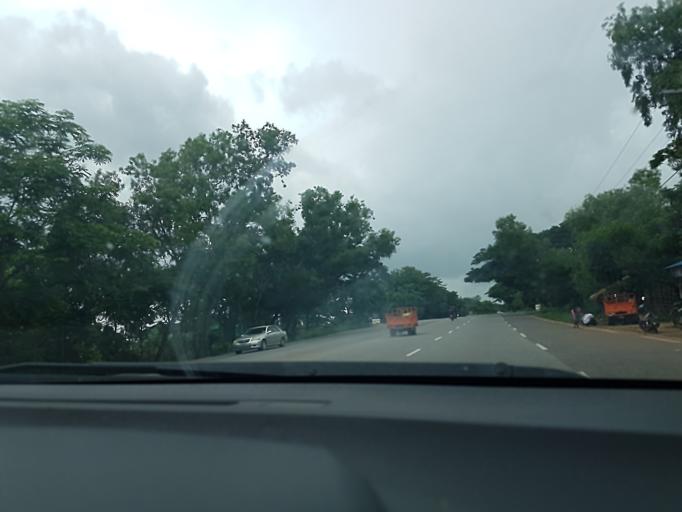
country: MM
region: Bago
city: Thanatpin
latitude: 17.1351
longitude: 96.2902
